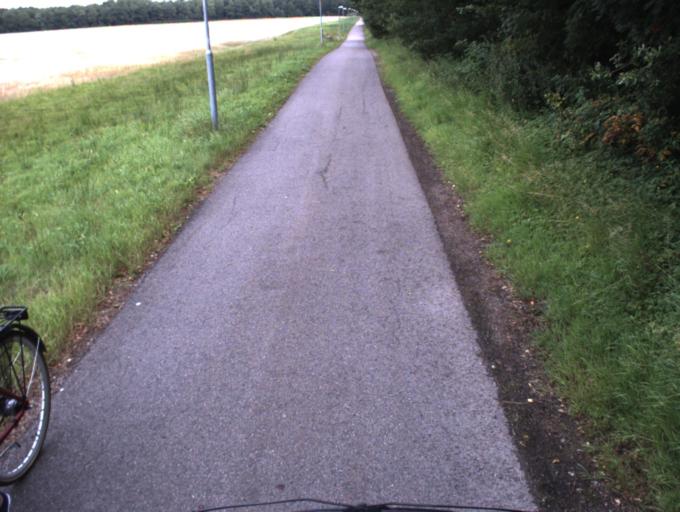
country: SE
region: Skane
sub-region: Helsingborg
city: Helsingborg
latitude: 56.0871
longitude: 12.6704
